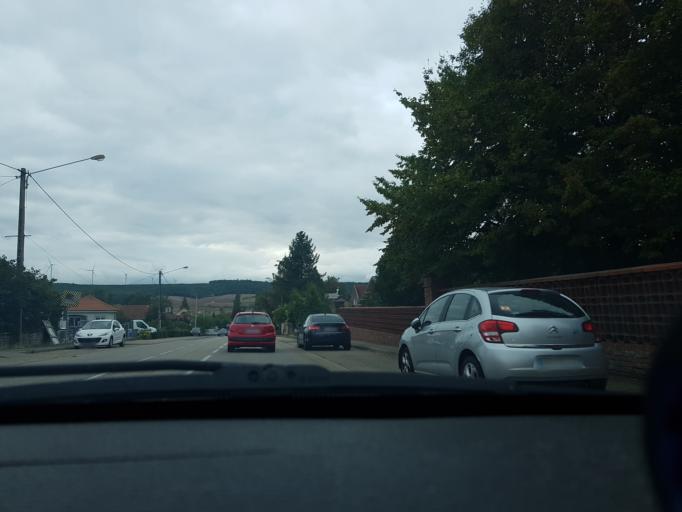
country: FR
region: Lorraine
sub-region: Departement de la Moselle
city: Chateau-Salins
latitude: 48.8250
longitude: 6.5056
